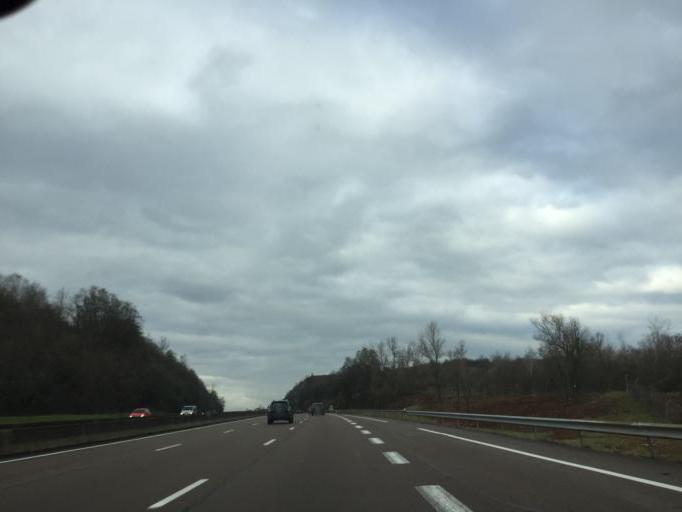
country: FR
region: Bourgogne
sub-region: Departement de Saone-et-Loire
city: Tournus
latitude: 46.5870
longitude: 4.9002
